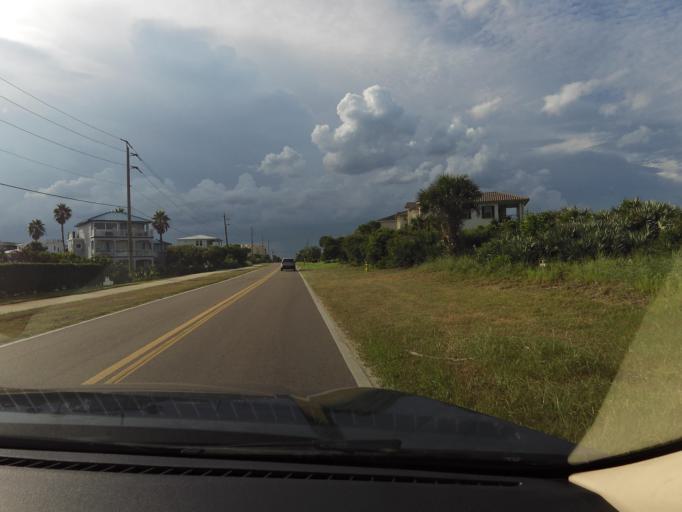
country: US
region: Florida
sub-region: Volusia County
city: Ponce Inlet
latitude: 29.0866
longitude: -80.9276
